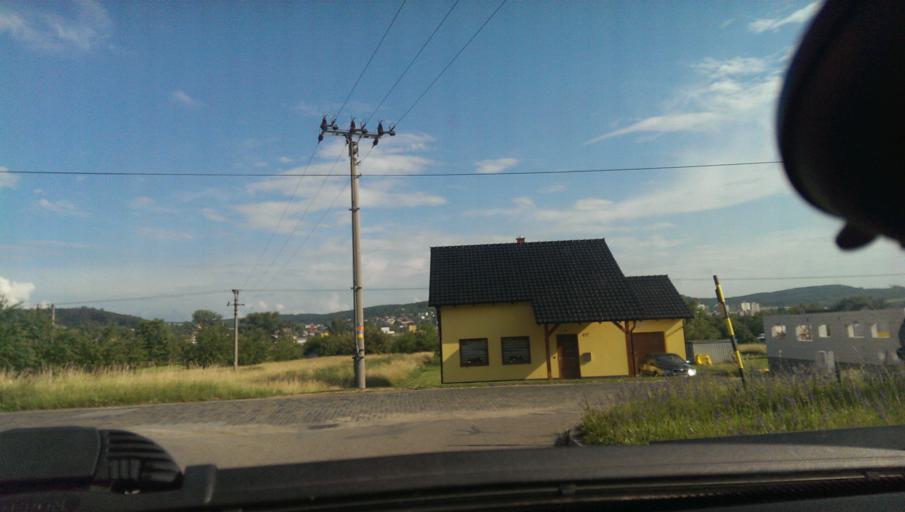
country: CZ
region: Zlin
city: Tecovice
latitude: 49.2167
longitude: 17.5860
